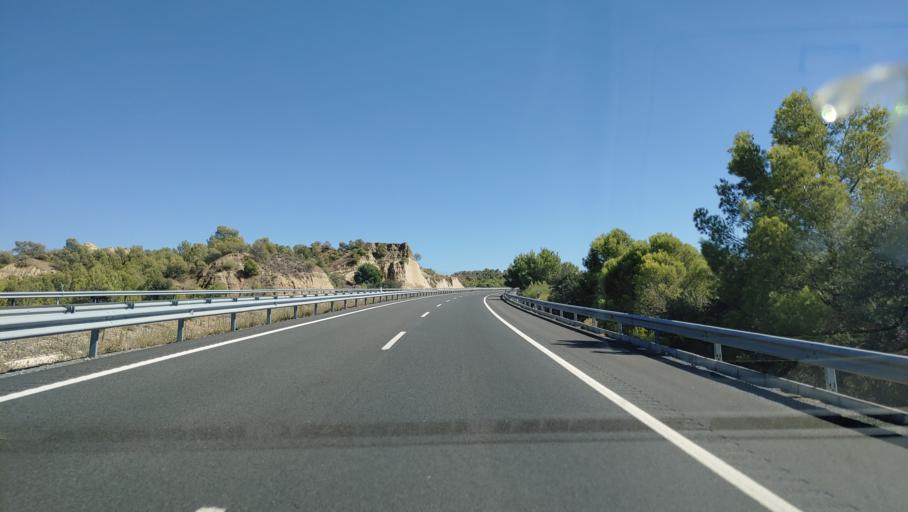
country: ES
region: Andalusia
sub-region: Provincia de Granada
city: Guadix
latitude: 37.2830
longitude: -3.0999
